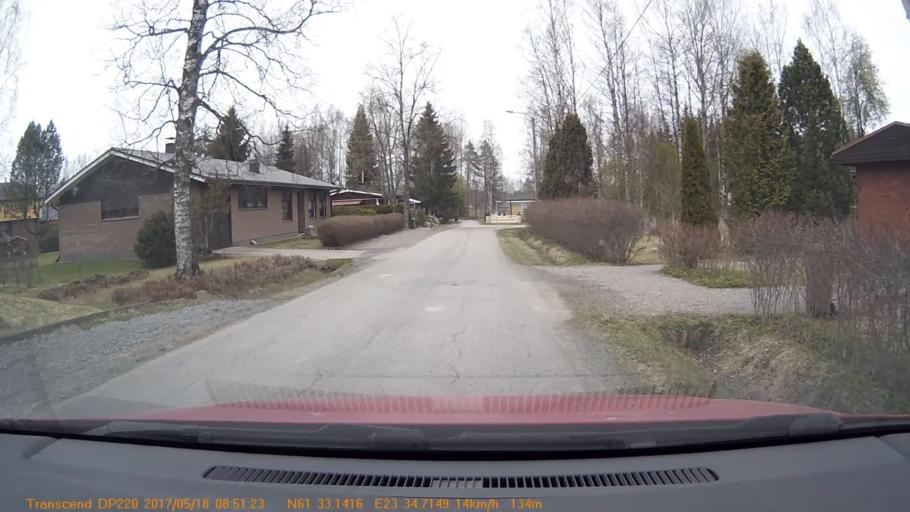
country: FI
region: Pirkanmaa
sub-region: Tampere
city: Yloejaervi
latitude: 61.5524
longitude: 23.5786
